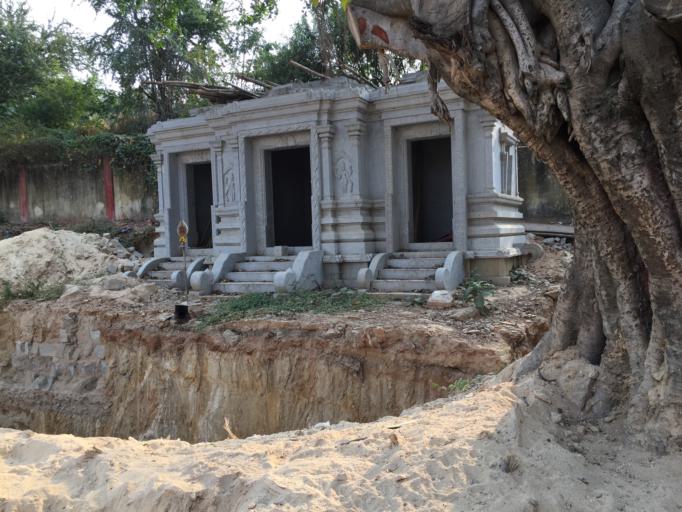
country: IN
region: Karnataka
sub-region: Bangalore Urban
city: Bangalore
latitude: 12.9577
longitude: 77.6359
